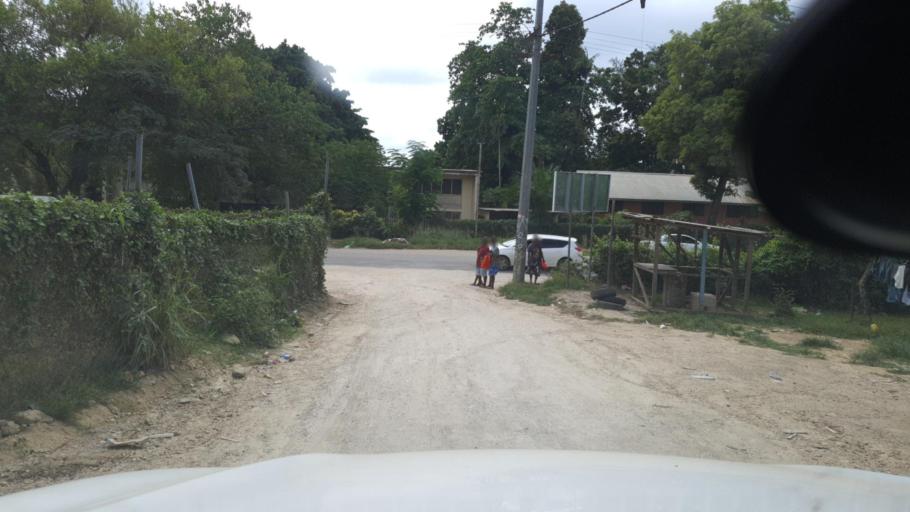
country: SB
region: Guadalcanal
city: Honiara
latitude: -9.4246
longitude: 159.9245
